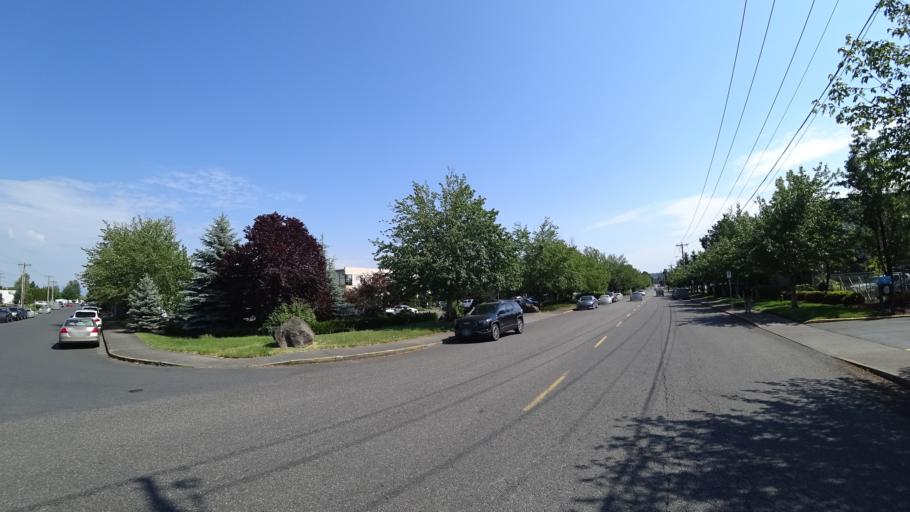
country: US
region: Washington
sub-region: Clark County
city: Mill Plain
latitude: 45.5643
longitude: -122.5212
